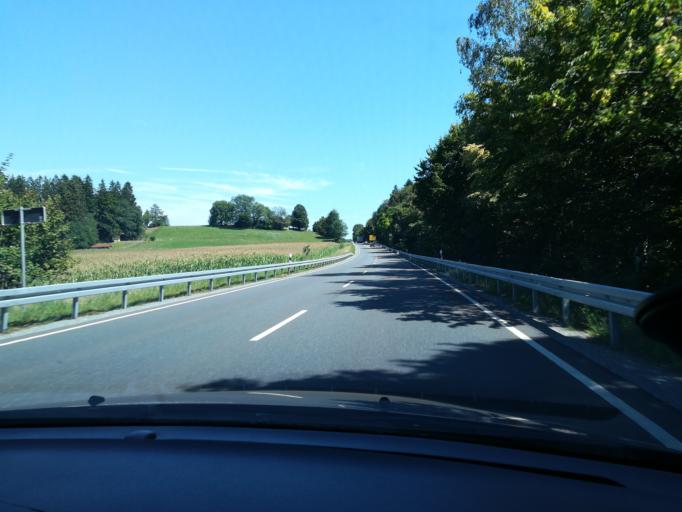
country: DE
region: Bavaria
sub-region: Upper Bavaria
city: Amerang
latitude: 48.0389
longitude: 12.3046
